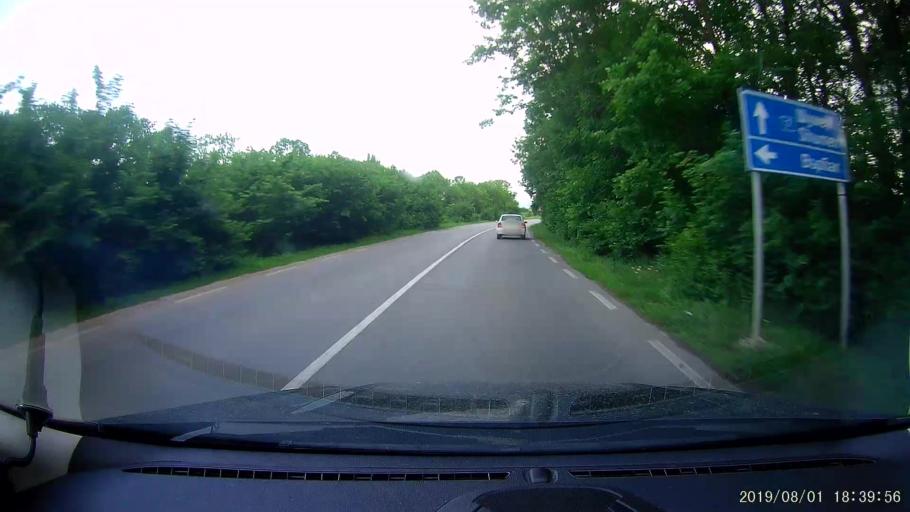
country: BG
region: Shumen
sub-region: Obshtina Khitrino
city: Gara Khitrino
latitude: 43.3757
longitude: 26.9196
